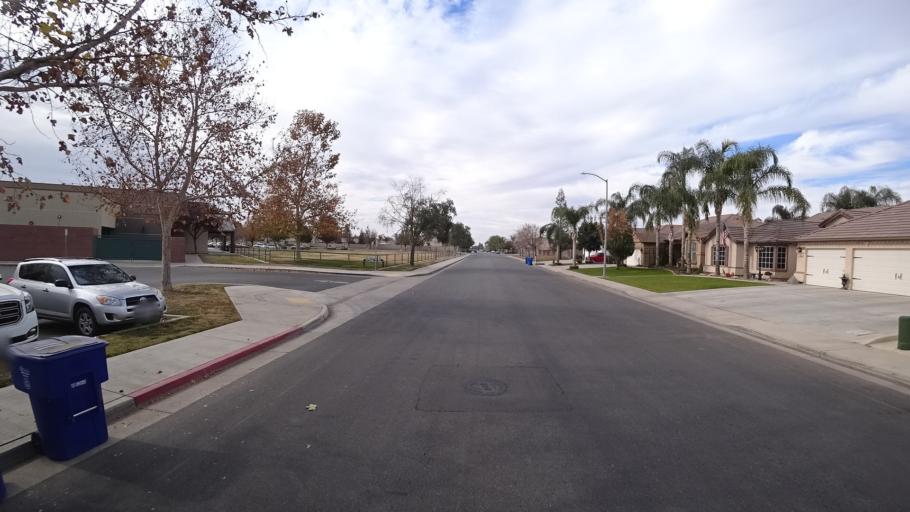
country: US
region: California
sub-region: Kern County
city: Rosedale
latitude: 35.4252
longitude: -119.1350
